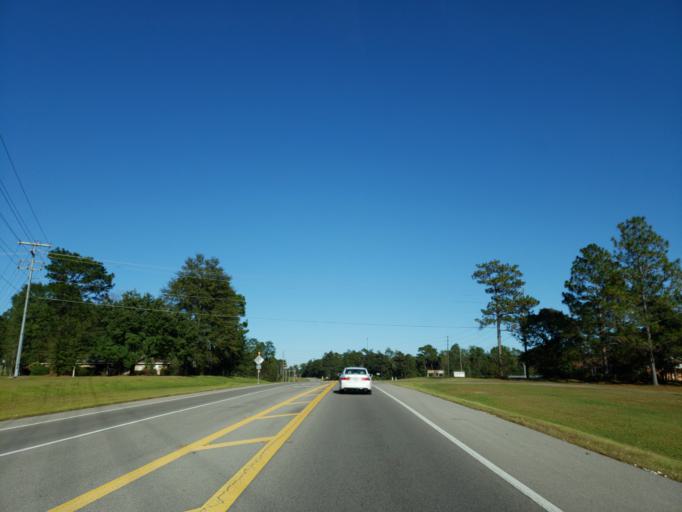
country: US
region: Mississippi
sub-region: Forrest County
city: Petal
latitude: 31.3521
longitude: -89.1739
